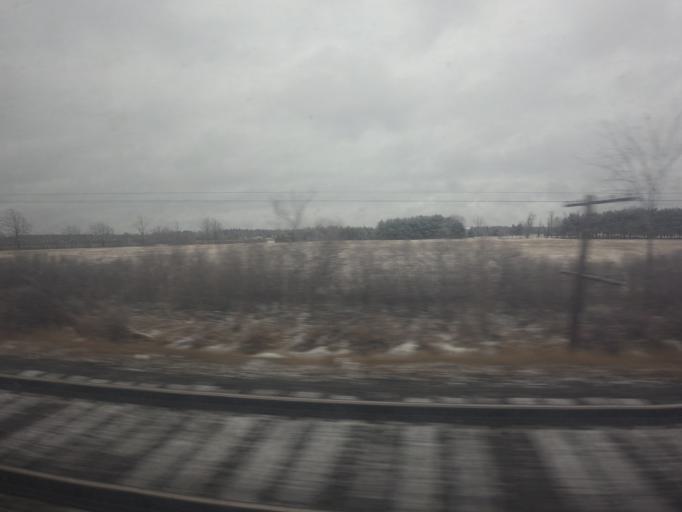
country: CA
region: Ontario
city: Gananoque
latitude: 44.3899
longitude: -76.0472
